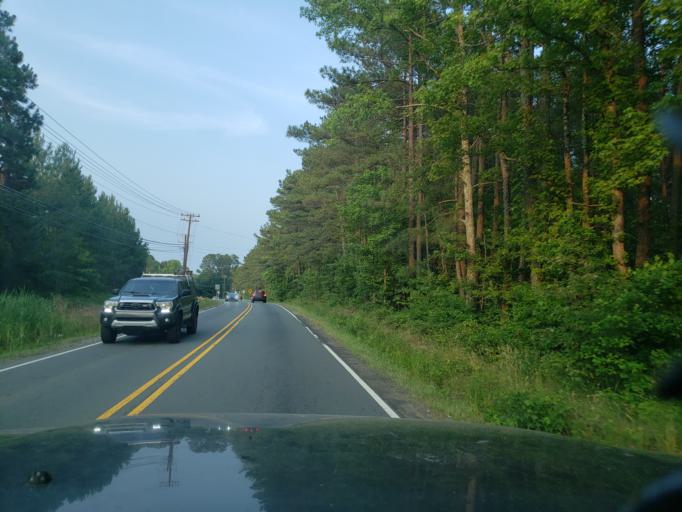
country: US
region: North Carolina
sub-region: Durham County
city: Durham
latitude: 35.9570
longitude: -78.8799
